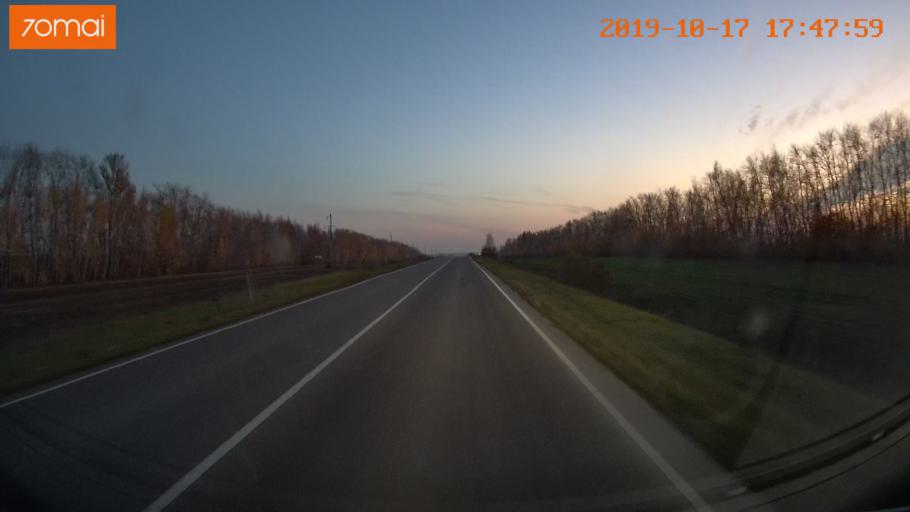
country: RU
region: Tula
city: Yepifan'
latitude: 53.6991
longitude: 38.6969
